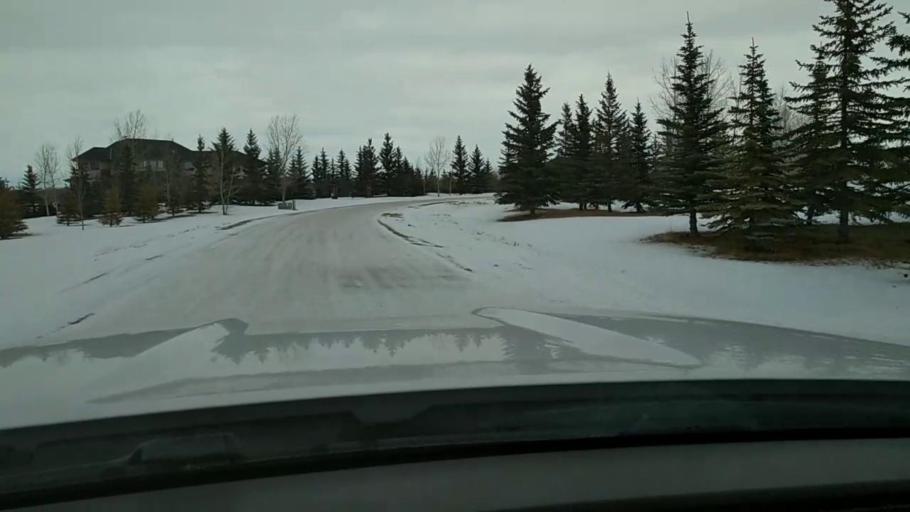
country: CA
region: Alberta
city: Cochrane
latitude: 51.2035
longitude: -114.2863
